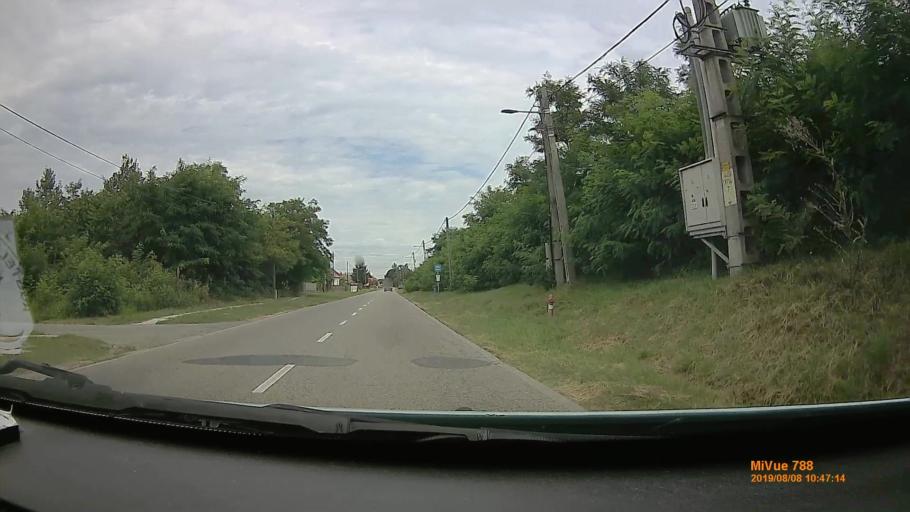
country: HU
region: Szabolcs-Szatmar-Bereg
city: Balkany
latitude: 47.7597
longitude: 21.8624
